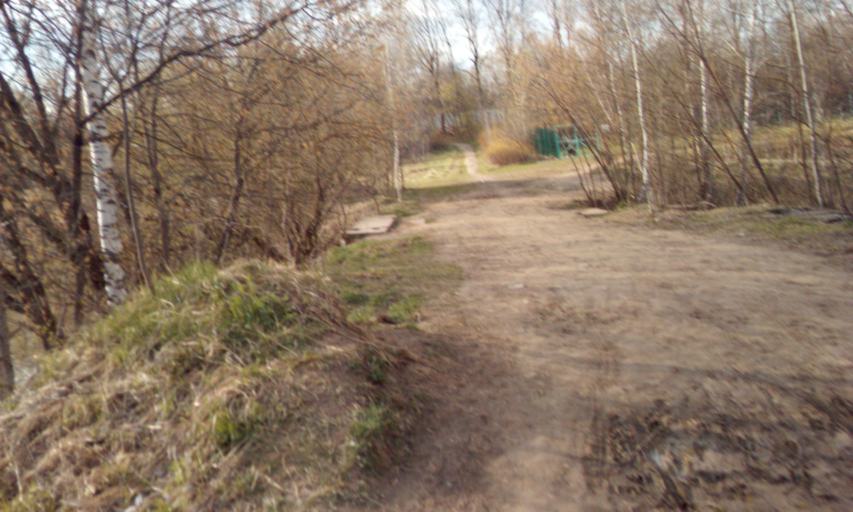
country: RU
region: Moscow
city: Novo-Peredelkino
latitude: 55.6461
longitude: 37.3319
